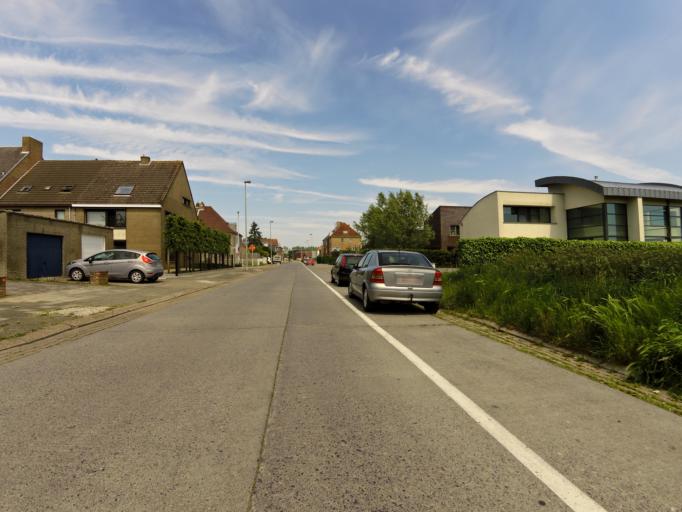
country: BE
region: Flanders
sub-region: Provincie West-Vlaanderen
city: Ostend
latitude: 51.2064
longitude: 2.8870
